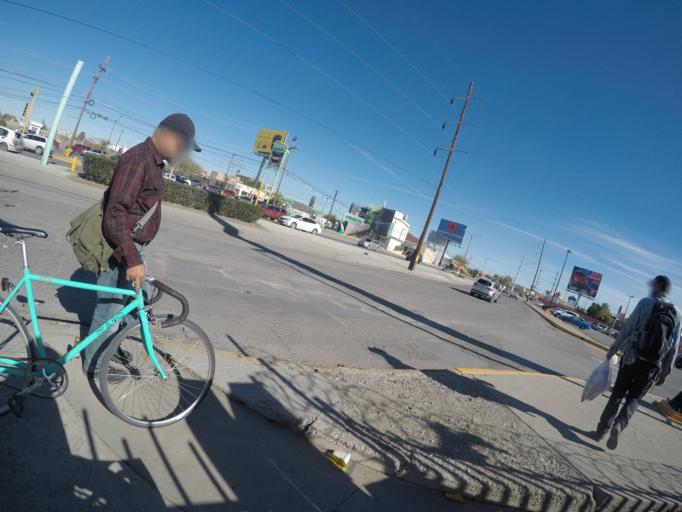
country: MX
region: Chihuahua
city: Ciudad Juarez
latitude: 31.7326
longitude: -106.4143
